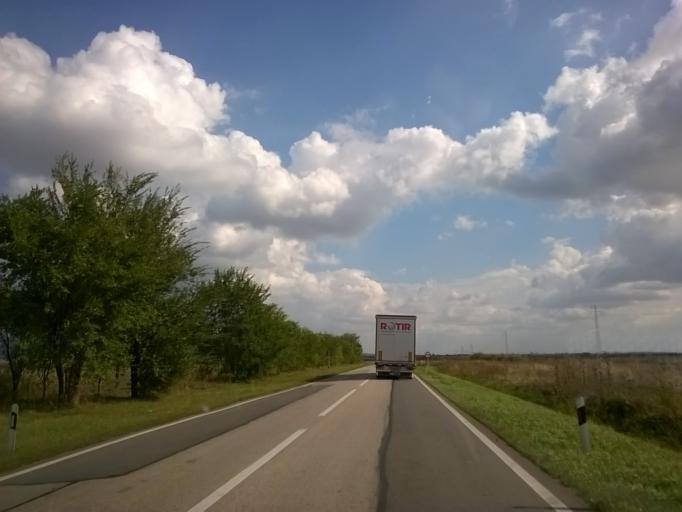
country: RS
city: Pavlis
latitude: 45.1604
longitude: 21.2398
